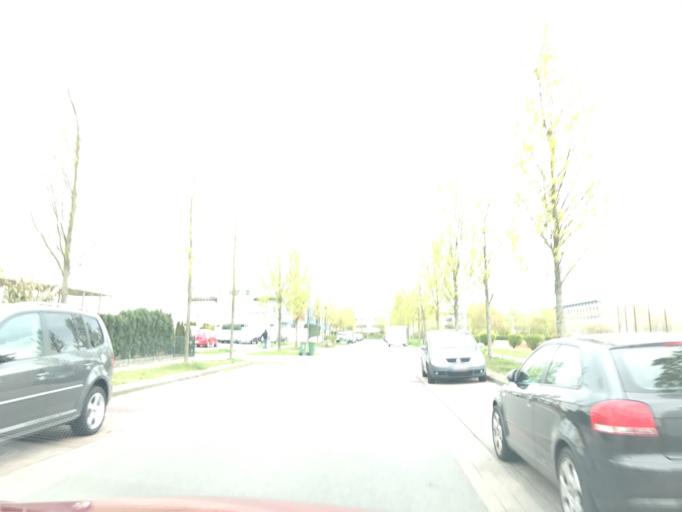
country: DE
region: Schleswig-Holstein
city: Oststeinbek
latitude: 53.4833
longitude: 10.1519
